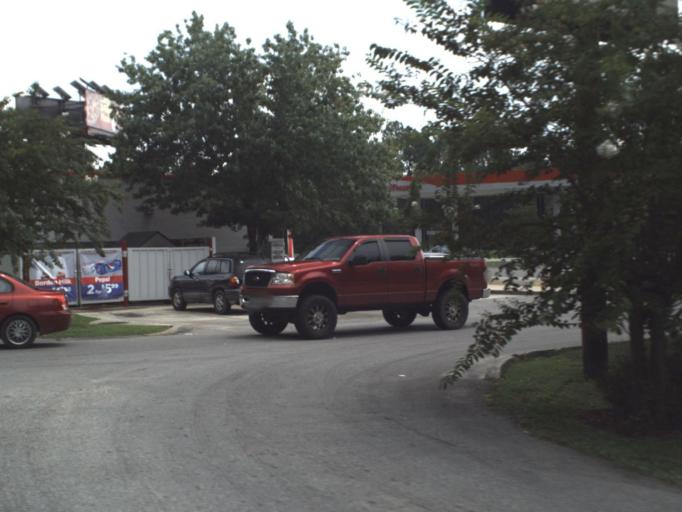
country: US
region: Florida
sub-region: Bay County
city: Hiland Park
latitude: 30.2336
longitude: -85.5807
